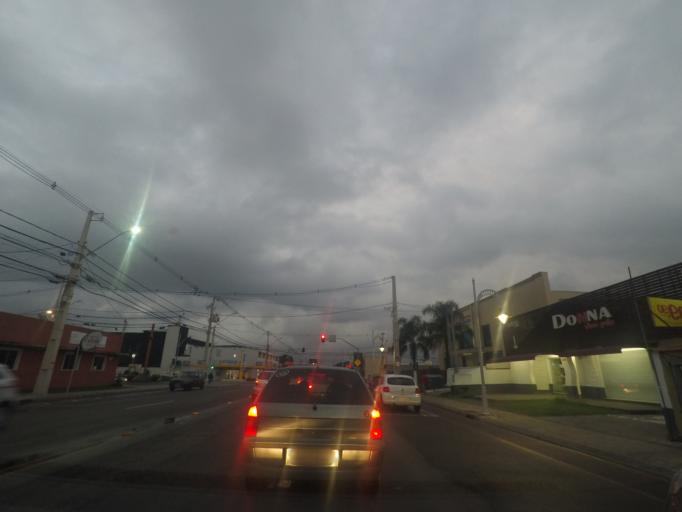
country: BR
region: Parana
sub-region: Curitiba
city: Curitiba
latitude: -25.4005
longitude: -49.3351
